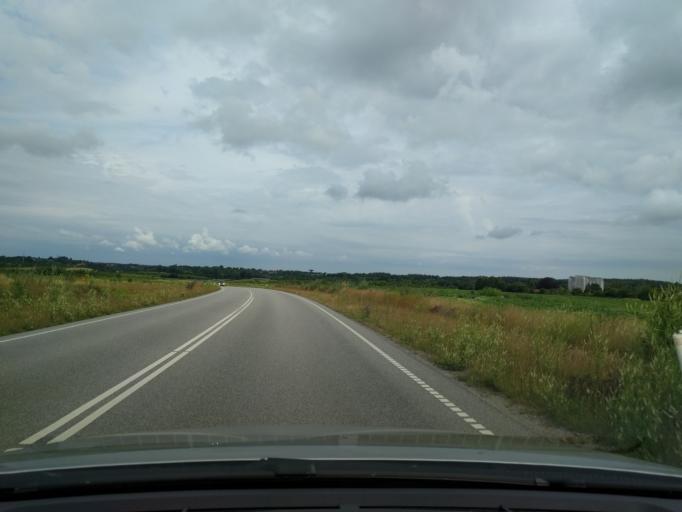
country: DK
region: Zealand
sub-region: Naestved Kommune
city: Naestved
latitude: 55.2116
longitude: 11.8128
